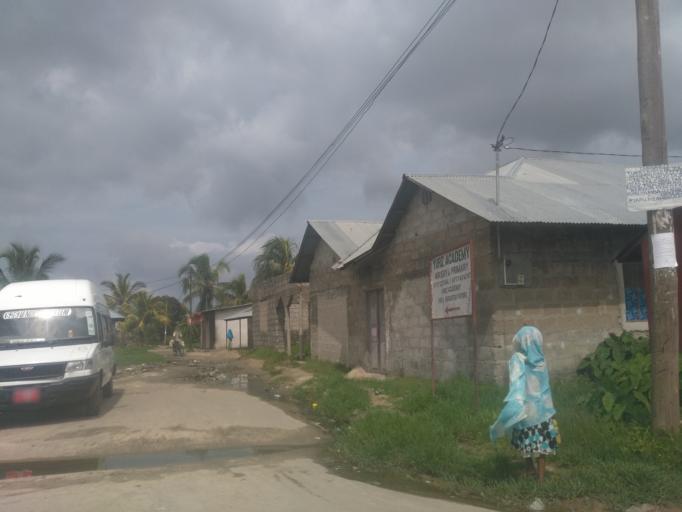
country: TZ
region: Zanzibar Urban/West
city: Zanzibar
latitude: -6.1764
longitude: 39.2398
